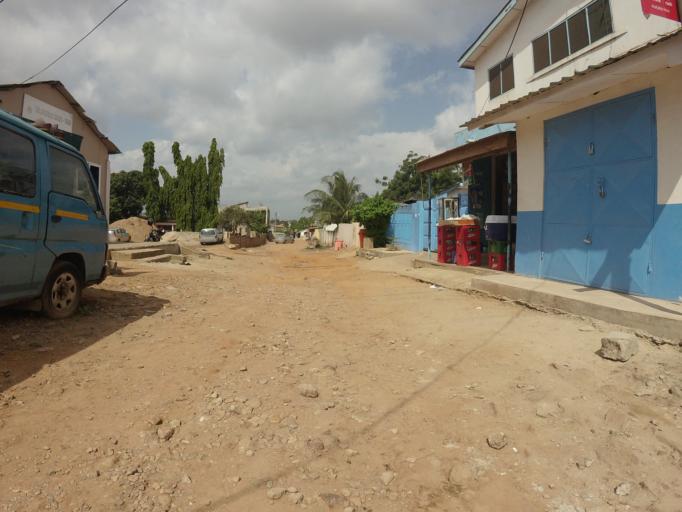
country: GH
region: Greater Accra
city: Dome
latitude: 5.6159
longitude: -0.2452
